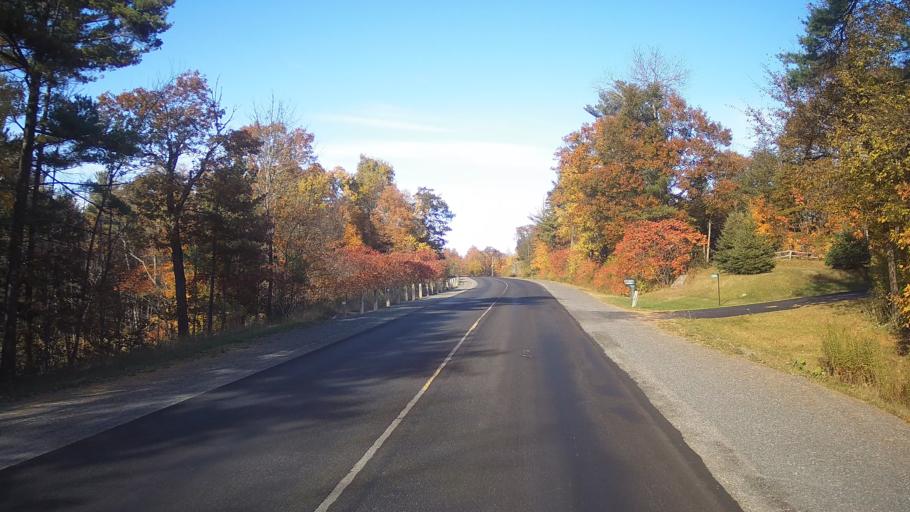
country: CA
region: Ontario
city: Kingston
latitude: 44.5319
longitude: -76.4496
